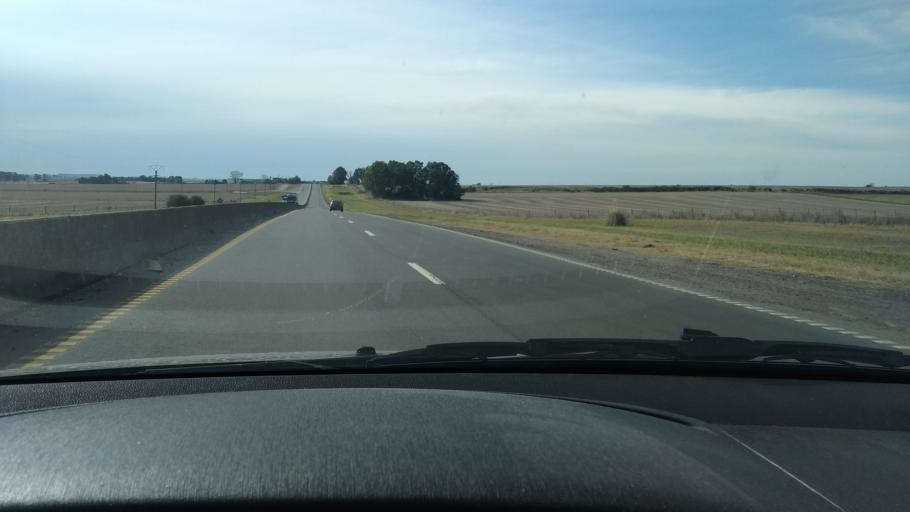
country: AR
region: Buenos Aires
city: Olavarria
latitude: -36.8971
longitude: -60.1678
